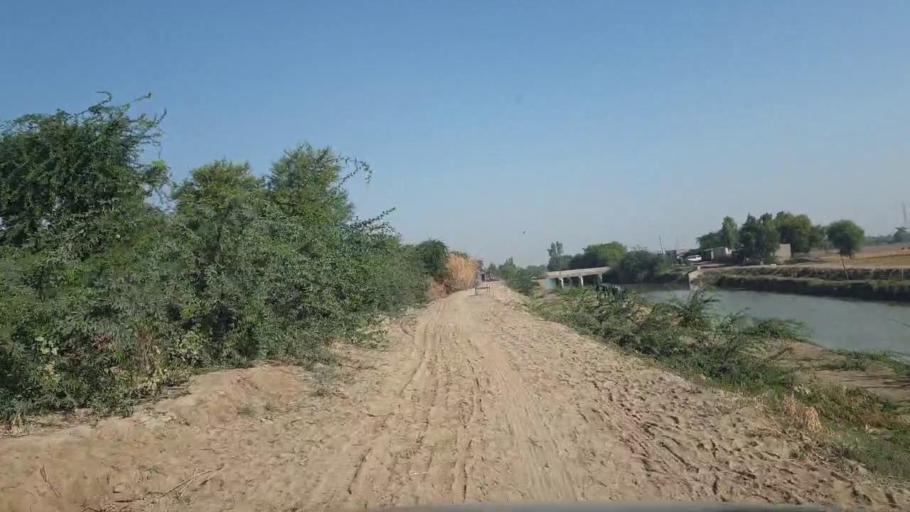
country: PK
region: Sindh
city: Badin
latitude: 24.7302
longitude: 68.8052
